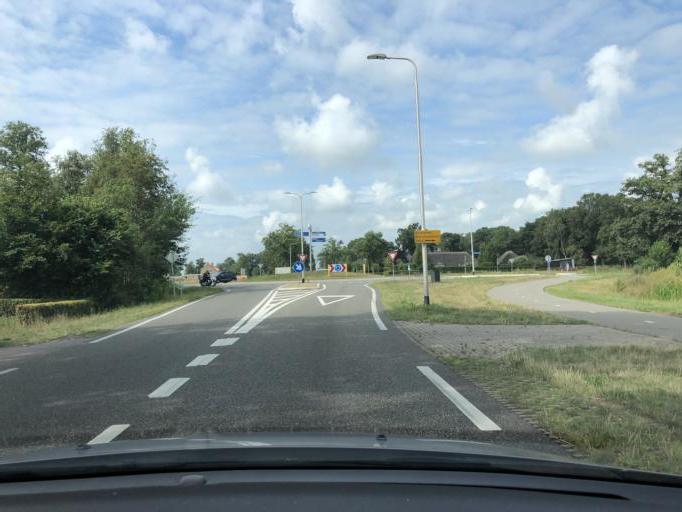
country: NL
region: Overijssel
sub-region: Gemeente Dalfsen
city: Dalfsen
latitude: 52.5647
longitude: 6.2630
